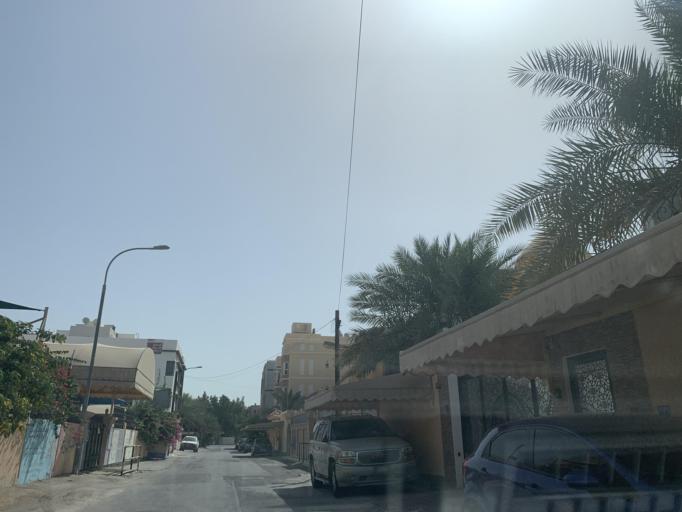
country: BH
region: Northern
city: Ar Rifa'
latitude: 26.1501
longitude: 50.5789
